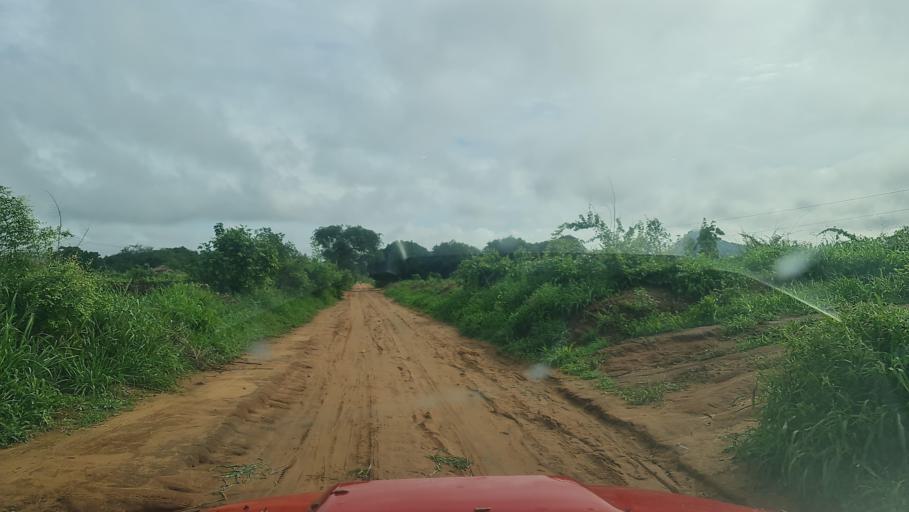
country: MW
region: Southern Region
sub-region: Nsanje District
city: Nsanje
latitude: -17.2811
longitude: 35.6151
